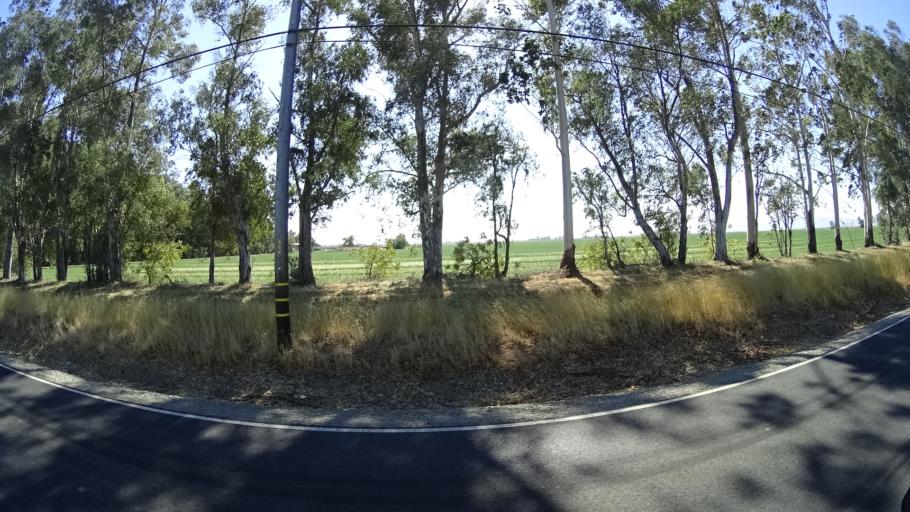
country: US
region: California
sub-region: Yolo County
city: Cottonwood
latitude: 38.6198
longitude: -121.8702
